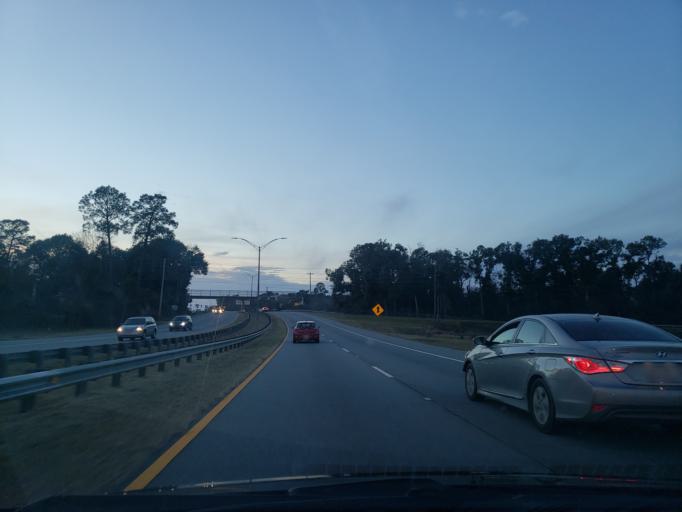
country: US
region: Georgia
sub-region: Dougherty County
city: Albany
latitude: 31.5722
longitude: -84.1138
